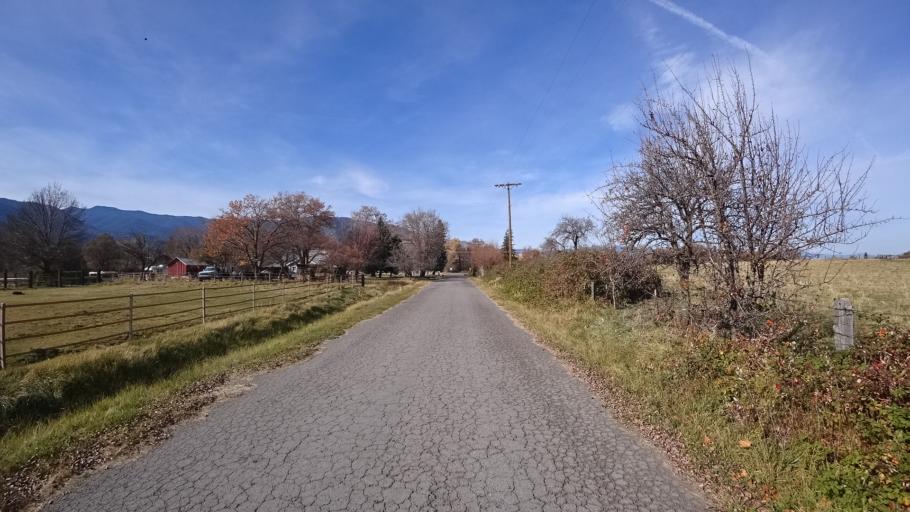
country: US
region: California
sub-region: Siskiyou County
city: Weed
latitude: 41.4470
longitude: -122.4284
